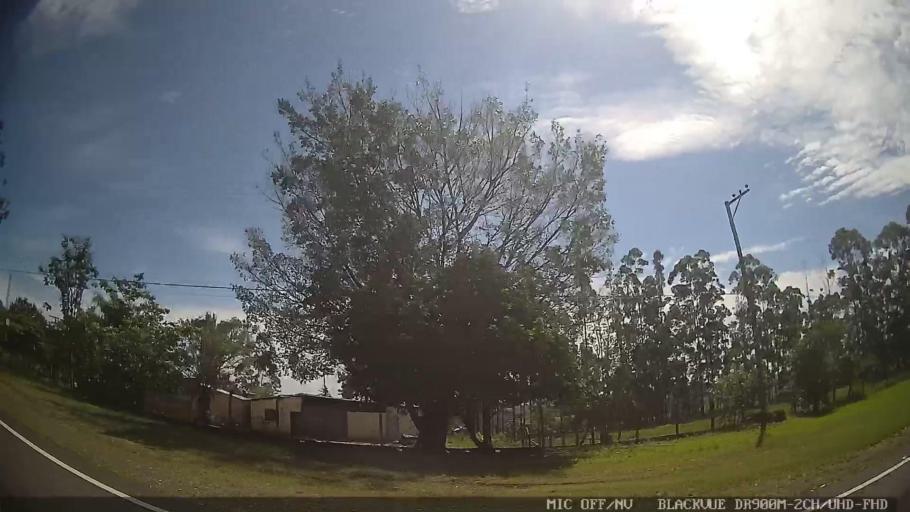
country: BR
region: Sao Paulo
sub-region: Boituva
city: Boituva
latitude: -23.1909
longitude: -47.6315
